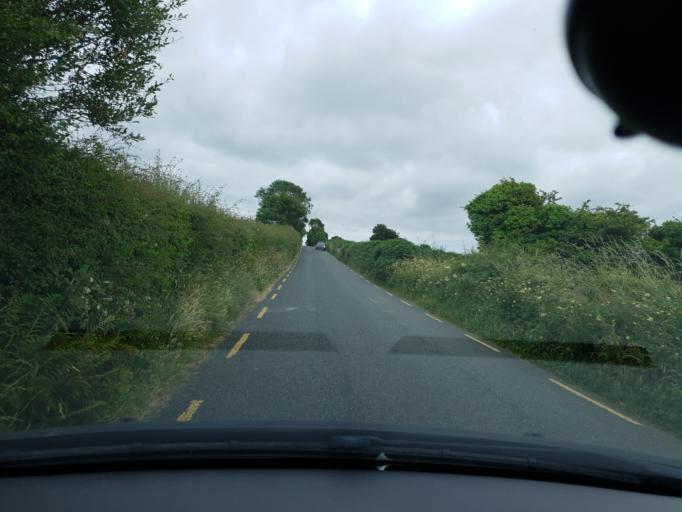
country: IE
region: Munster
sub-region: Ciarrai
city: Cill Airne
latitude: 52.1495
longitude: -9.5946
